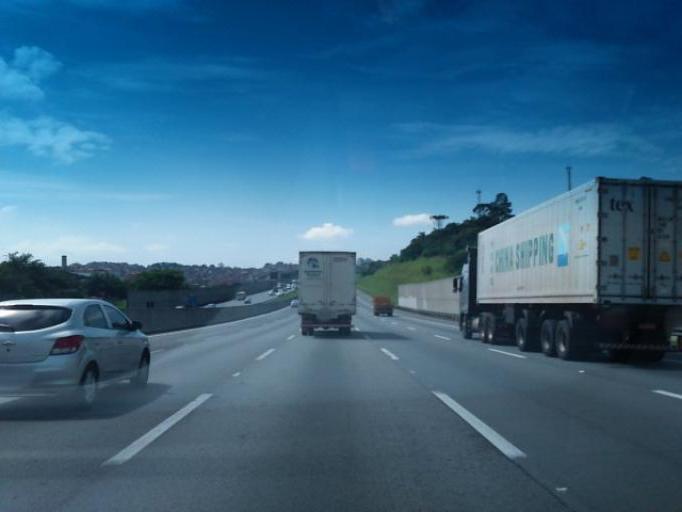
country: BR
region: Sao Paulo
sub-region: Osasco
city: Osasco
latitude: -23.5718
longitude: -46.8124
